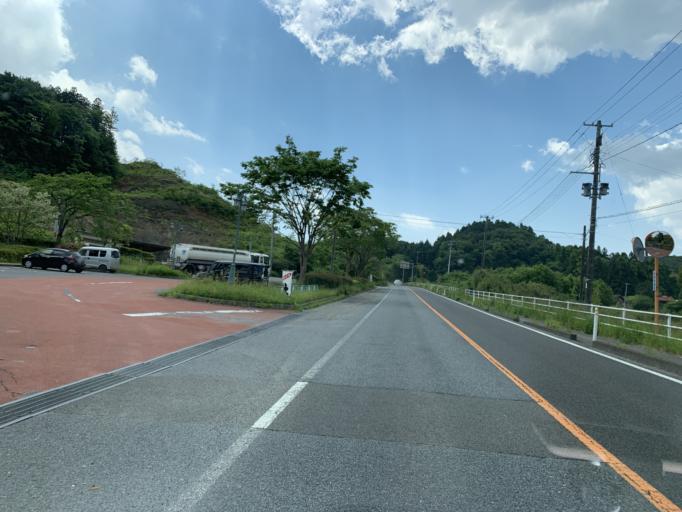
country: JP
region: Miyagi
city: Matsushima
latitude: 38.4203
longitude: 141.0590
